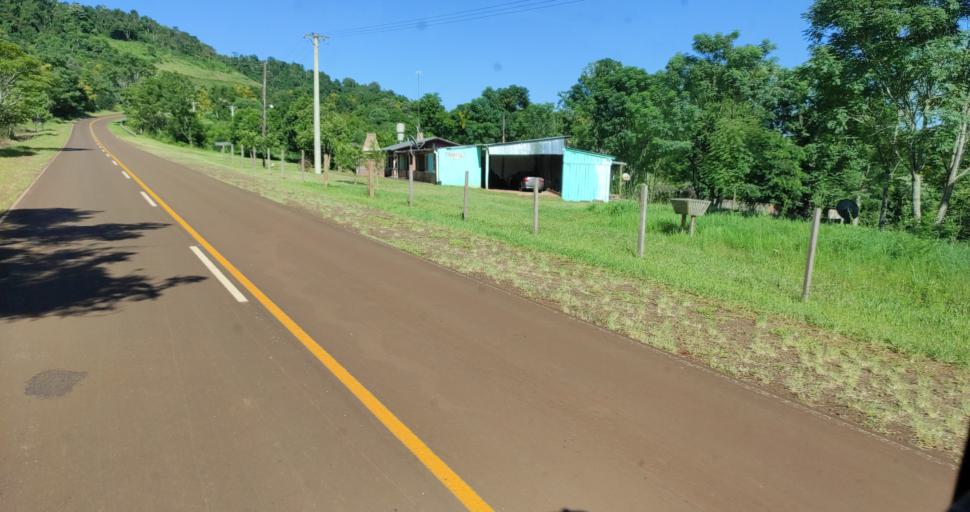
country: AR
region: Misiones
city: El Soberbio
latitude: -27.2248
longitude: -54.0571
